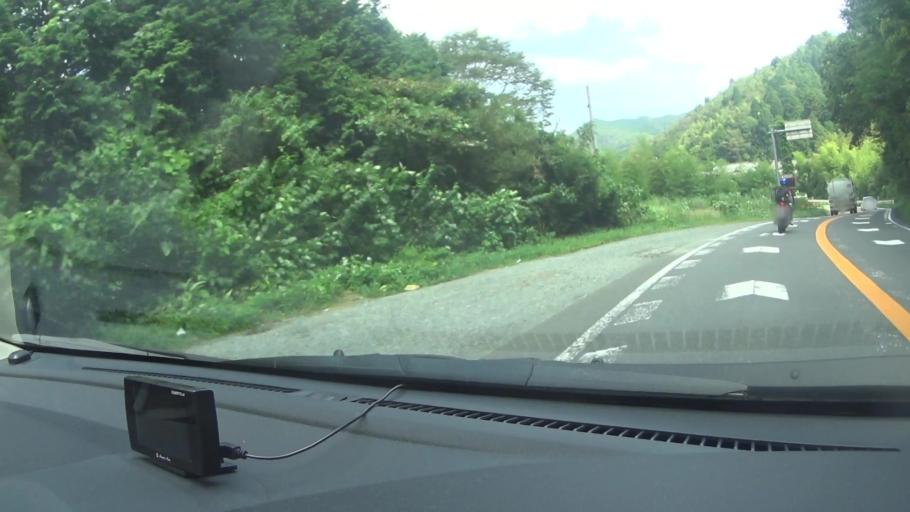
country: JP
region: Kyoto
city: Ayabe
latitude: 35.2529
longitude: 135.2771
